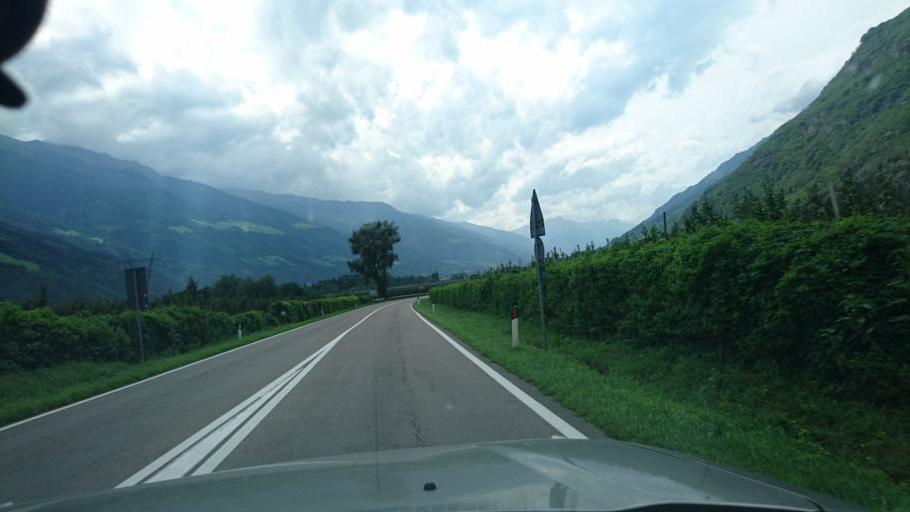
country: IT
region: Trentino-Alto Adige
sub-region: Bolzano
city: Rabla
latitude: 46.6682
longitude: 11.0582
